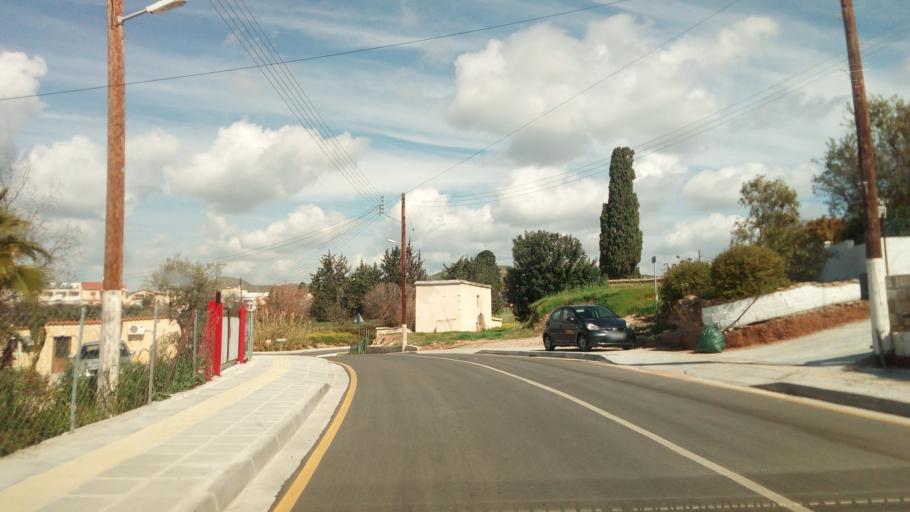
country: CY
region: Pafos
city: Mesogi
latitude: 34.7384
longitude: 32.5347
